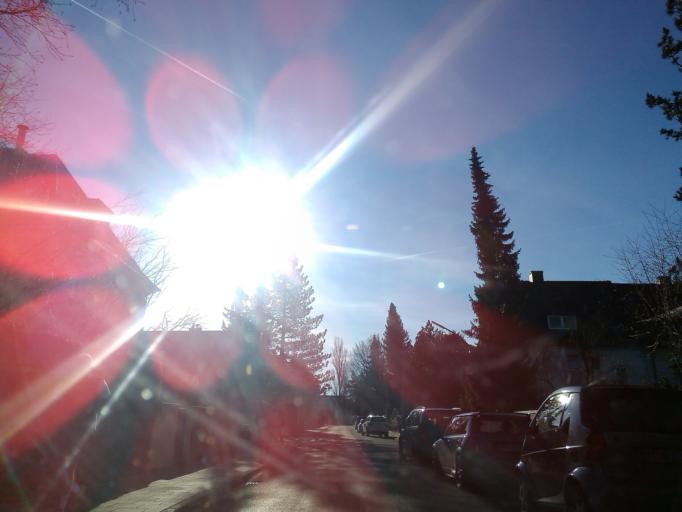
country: DE
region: Bavaria
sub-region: Upper Bavaria
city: Pasing
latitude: 48.1564
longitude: 11.4703
